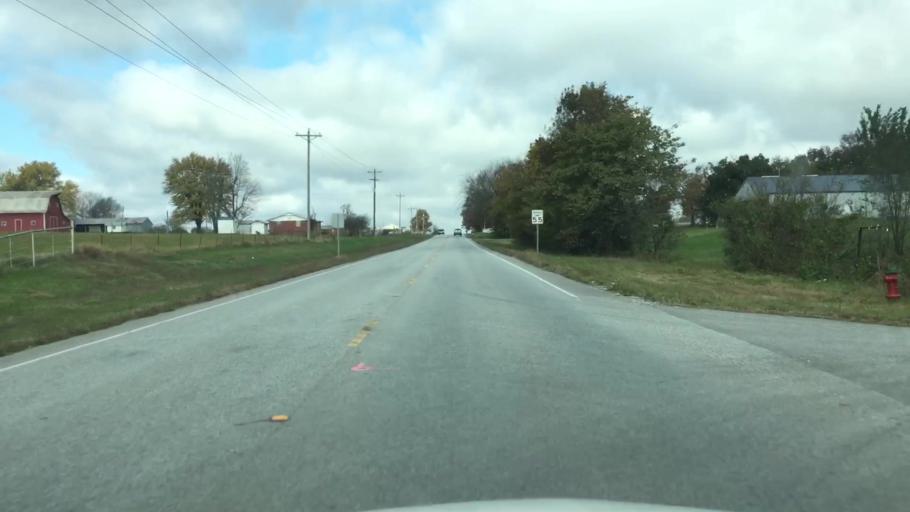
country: US
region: Arkansas
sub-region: Benton County
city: Centerton
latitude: 36.2654
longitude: -94.3504
